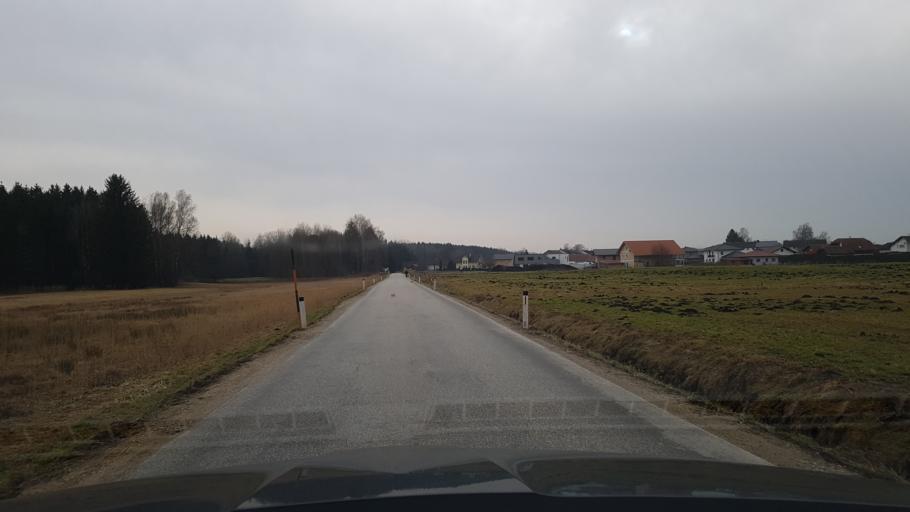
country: AT
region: Salzburg
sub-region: Politischer Bezirk Salzburg-Umgebung
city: Lamprechtshausen
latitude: 48.0484
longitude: 12.9531
